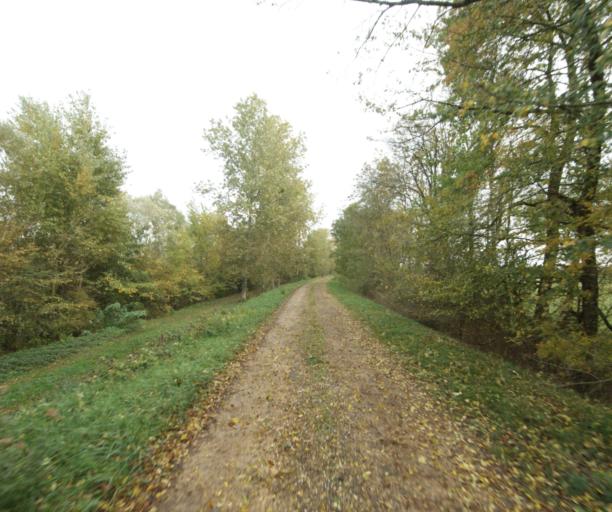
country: FR
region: Rhone-Alpes
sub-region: Departement de l'Ain
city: Pont-de-Vaux
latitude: 46.4564
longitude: 4.8986
